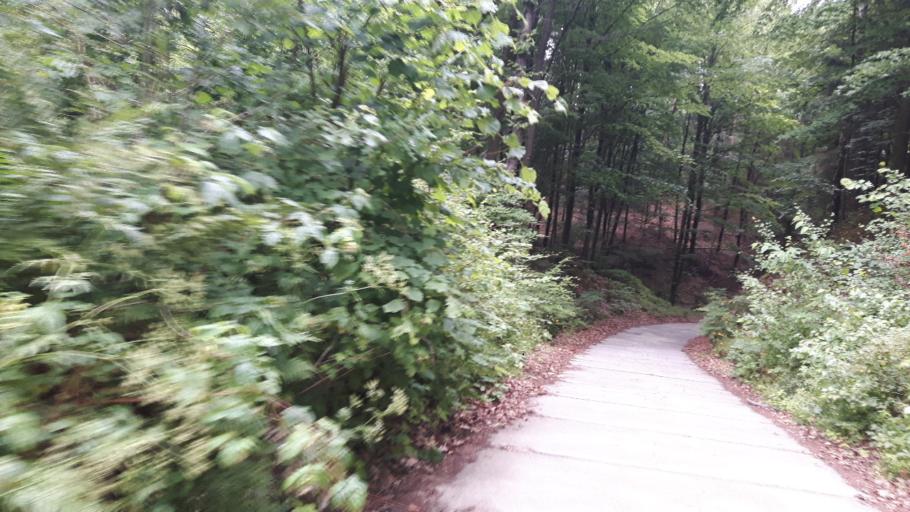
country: PL
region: Warmian-Masurian Voivodeship
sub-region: Powiat braniewski
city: Frombork
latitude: 54.3165
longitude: 19.6160
